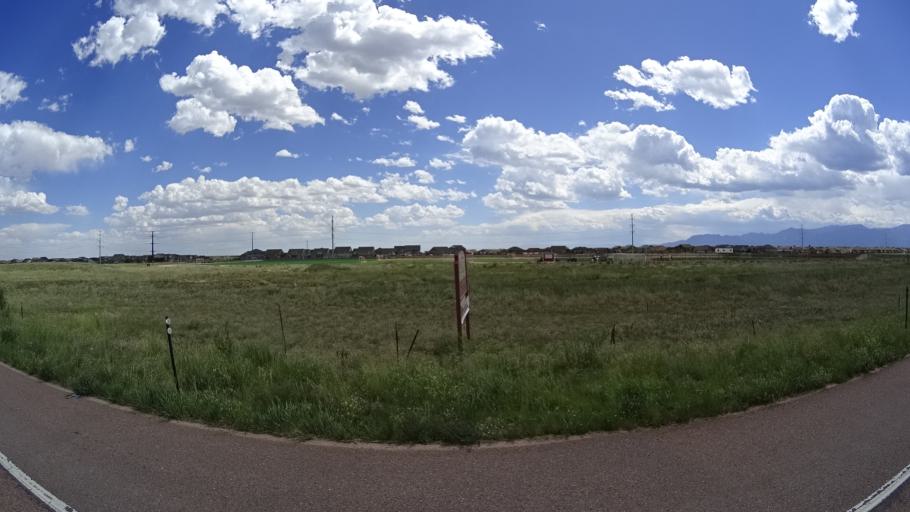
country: US
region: Colorado
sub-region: El Paso County
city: Black Forest
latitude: 38.9401
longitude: -104.6663
